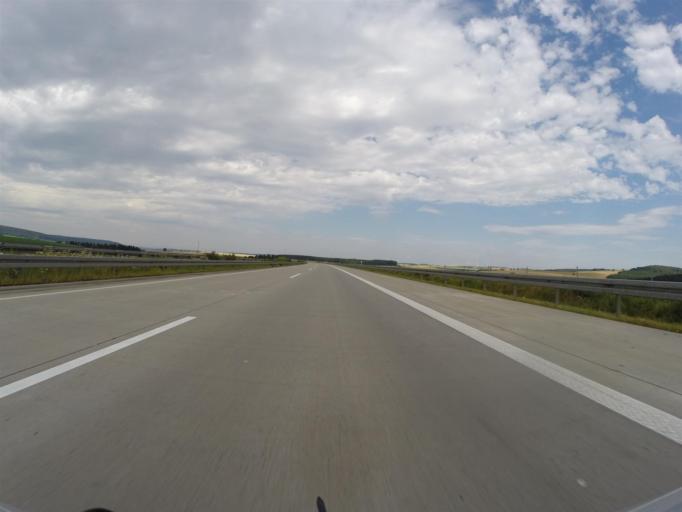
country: DE
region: Thuringia
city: Wingerode
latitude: 51.3980
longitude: 10.2613
